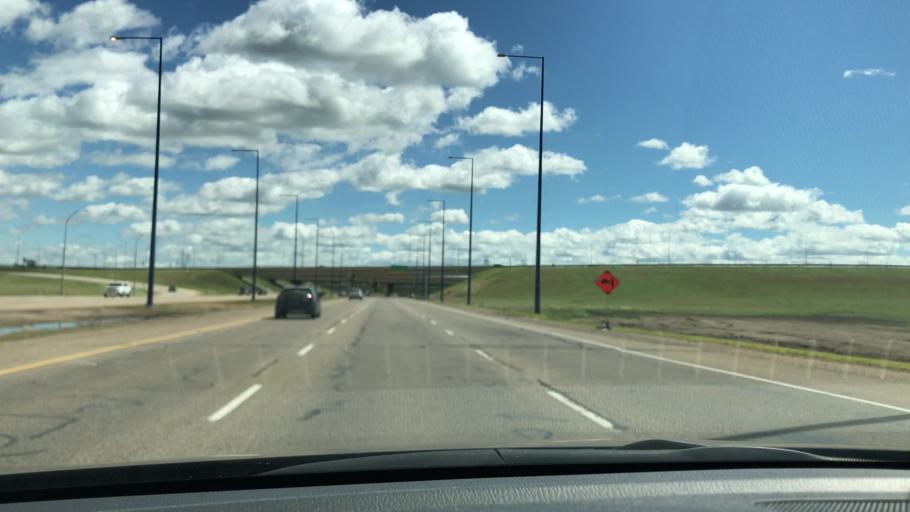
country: CA
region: Alberta
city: Edmonton
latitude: 53.4409
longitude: -113.4926
